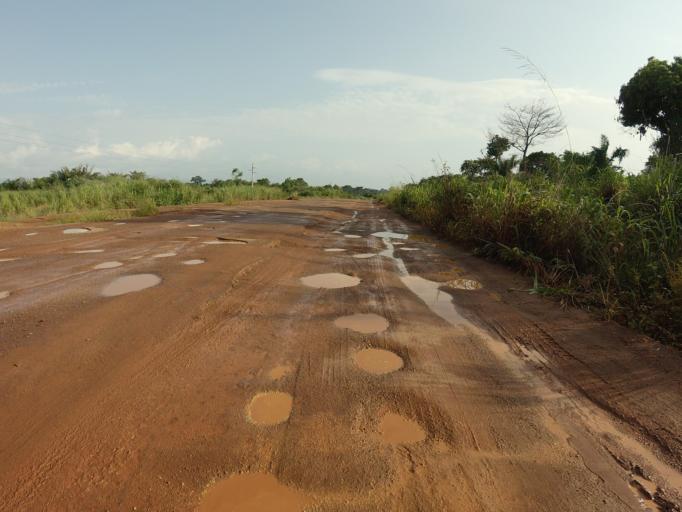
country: GH
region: Volta
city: Hohoe
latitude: 7.0649
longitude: 0.4333
